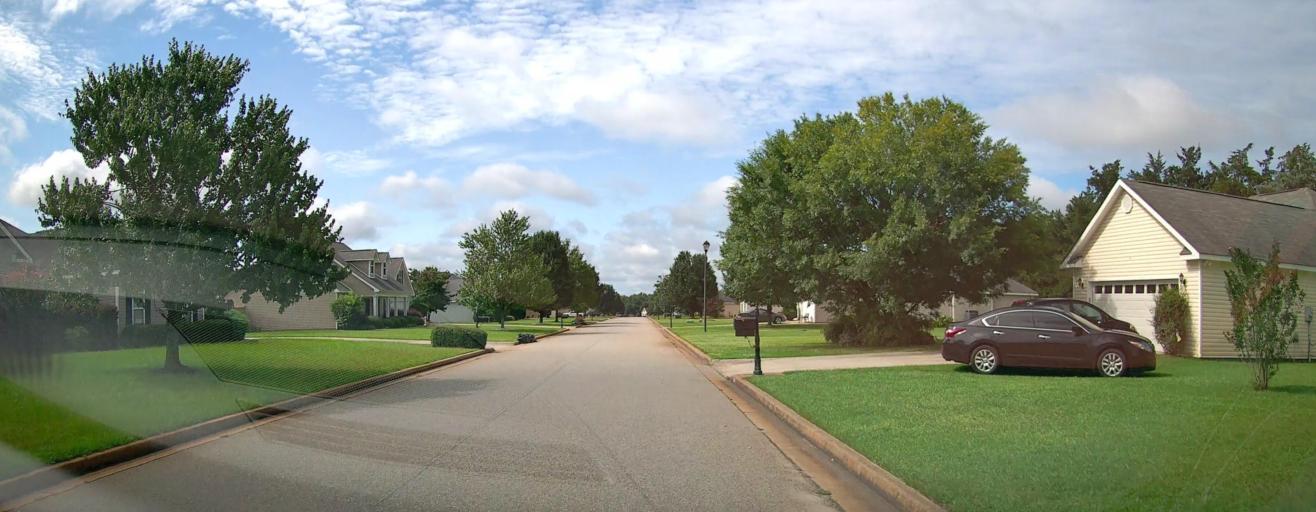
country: US
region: Georgia
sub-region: Peach County
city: Byron
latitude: 32.6509
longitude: -83.7257
